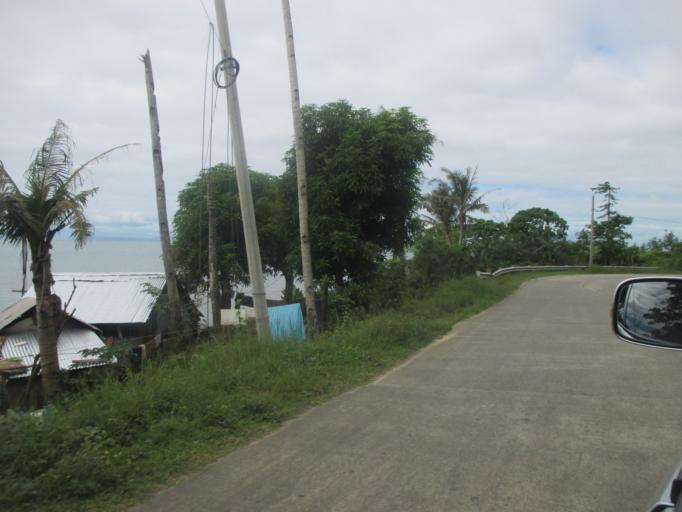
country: PH
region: Eastern Visayas
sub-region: Province of Eastern Samar
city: Lawa-an
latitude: 11.1117
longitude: 125.2110
